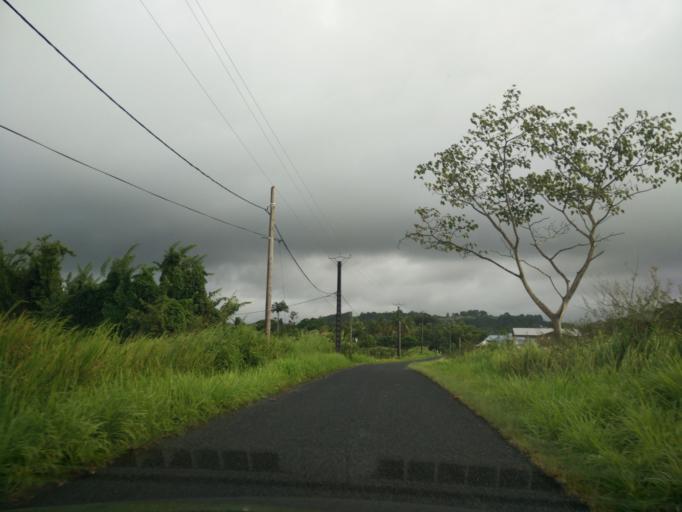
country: GP
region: Guadeloupe
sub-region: Guadeloupe
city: Petit-Bourg
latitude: 16.1752
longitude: -61.6214
